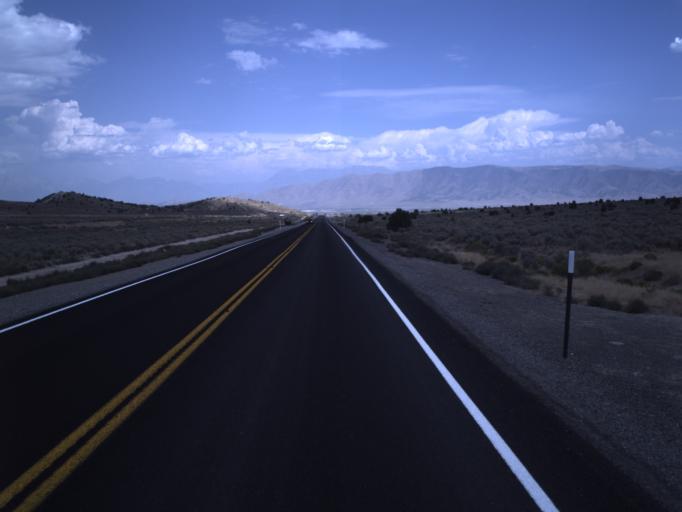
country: US
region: Utah
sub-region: Utah County
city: Eagle Mountain
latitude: 40.2325
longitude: -112.1749
